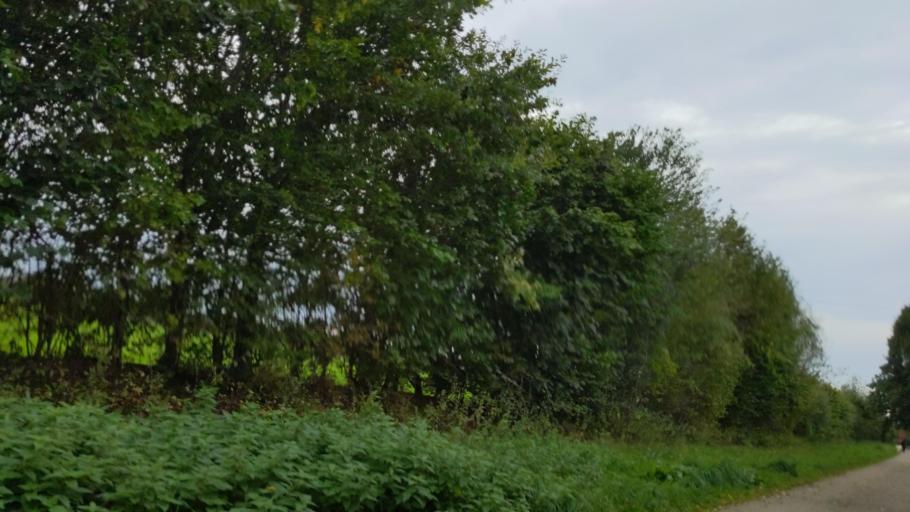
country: DE
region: Schleswig-Holstein
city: Gross Gronau
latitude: 53.8012
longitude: 10.7628
